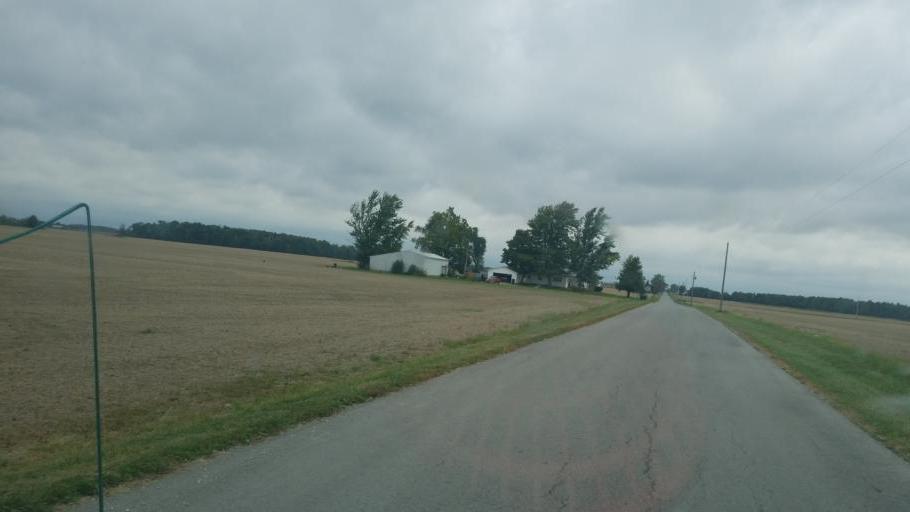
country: US
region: Ohio
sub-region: Seneca County
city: Fostoria
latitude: 41.0795
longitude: -83.5168
